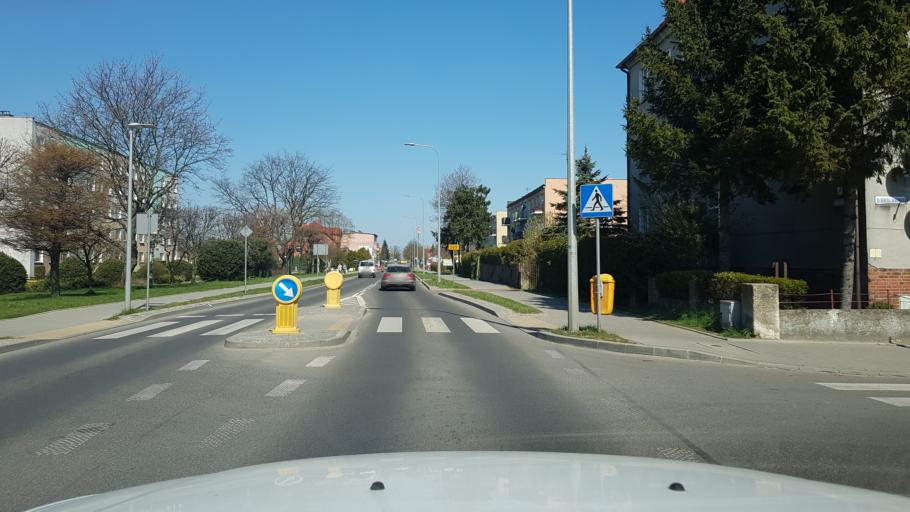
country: PL
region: West Pomeranian Voivodeship
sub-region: Powiat slawienski
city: Slawno
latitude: 54.3593
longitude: 16.6741
